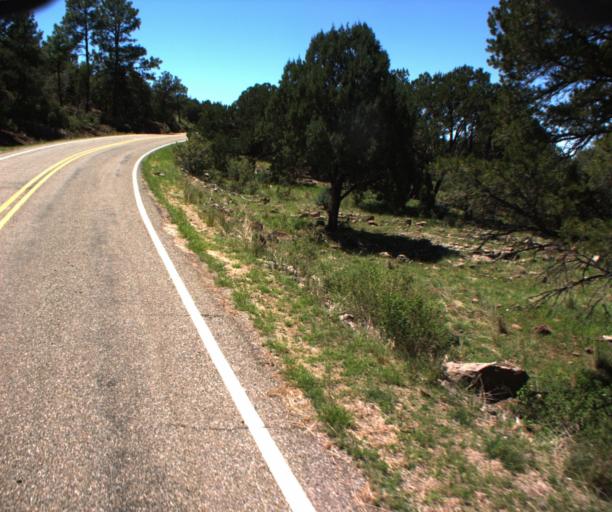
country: US
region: Arizona
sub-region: Greenlee County
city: Morenci
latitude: 33.2701
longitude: -109.3596
